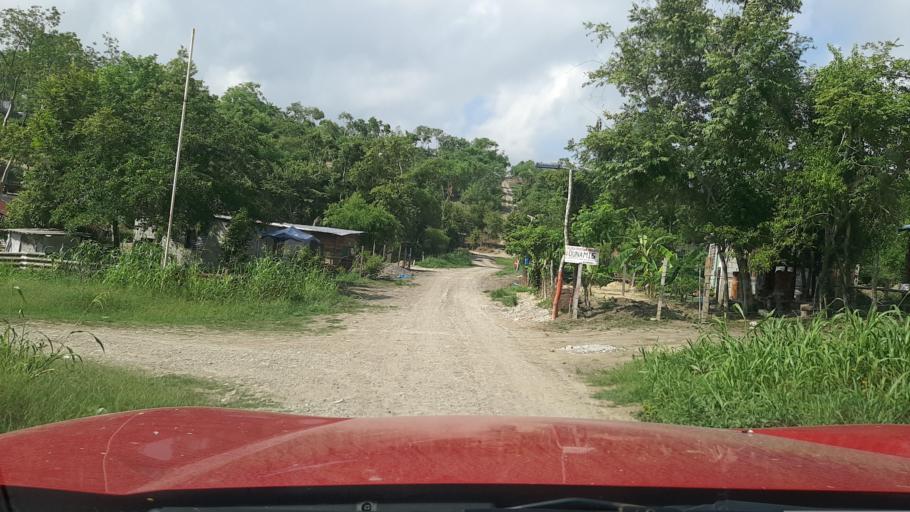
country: MX
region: Veracruz
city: Coatzintla
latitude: 20.5045
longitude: -97.4598
